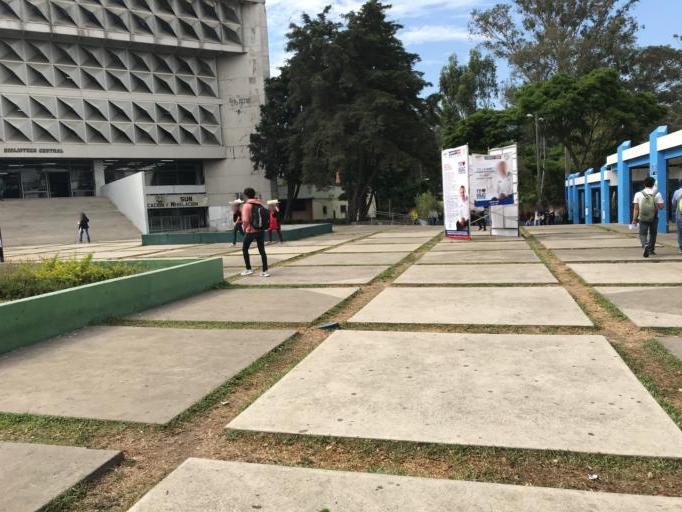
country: GT
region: Guatemala
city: Santa Catarina Pinula
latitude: 14.5874
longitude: -90.5522
